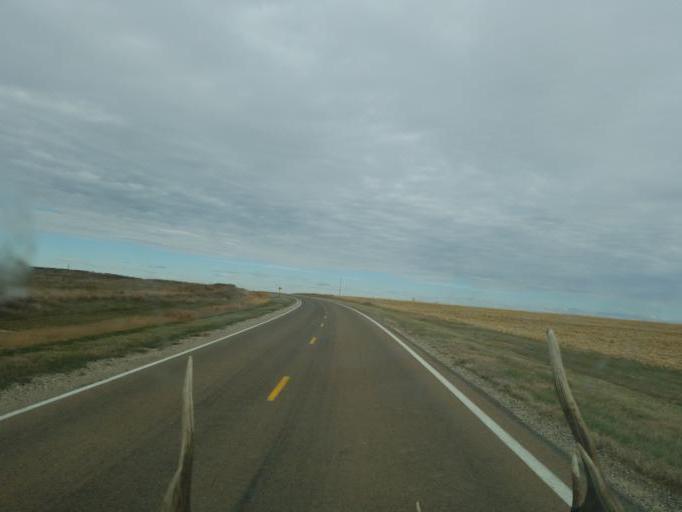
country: US
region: Kansas
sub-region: Logan County
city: Oakley
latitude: 39.0366
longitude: -101.2750
